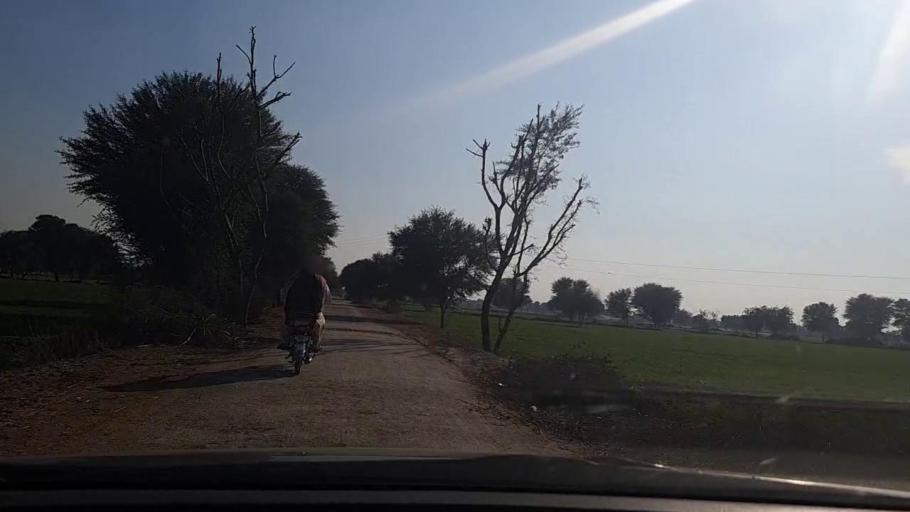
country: PK
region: Sindh
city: Sehwan
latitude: 26.3207
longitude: 68.0062
